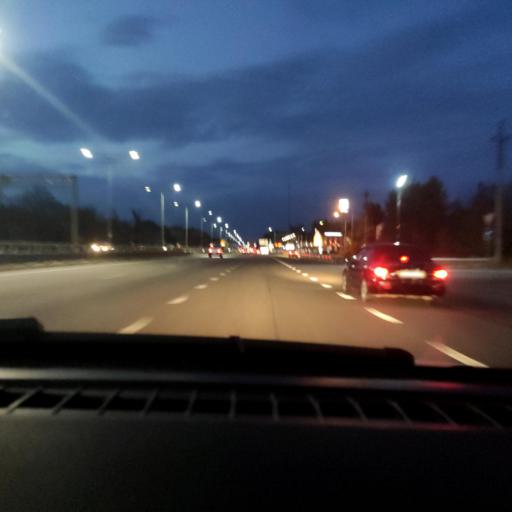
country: RU
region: Voronezj
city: Podgornoye
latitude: 51.8458
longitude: 39.2148
